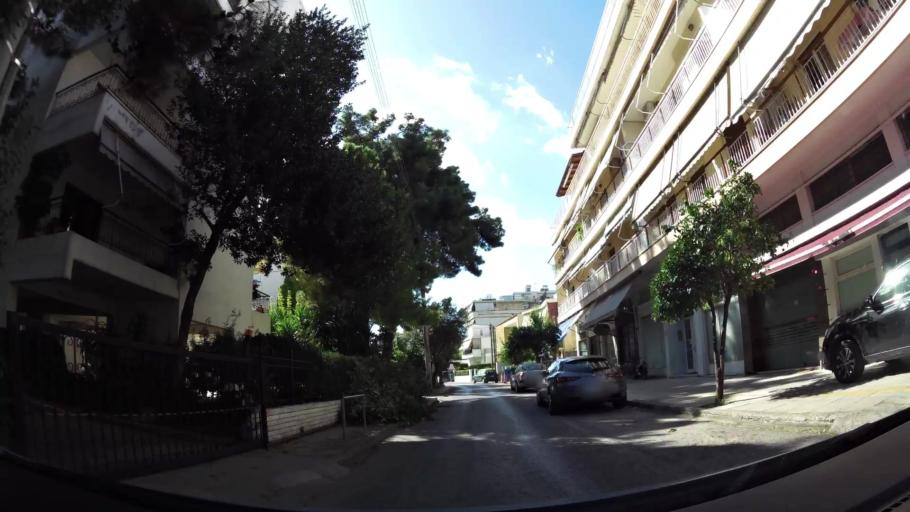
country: GR
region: Attica
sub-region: Nomarchia Athinas
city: Cholargos
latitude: 38.0099
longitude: 23.7946
